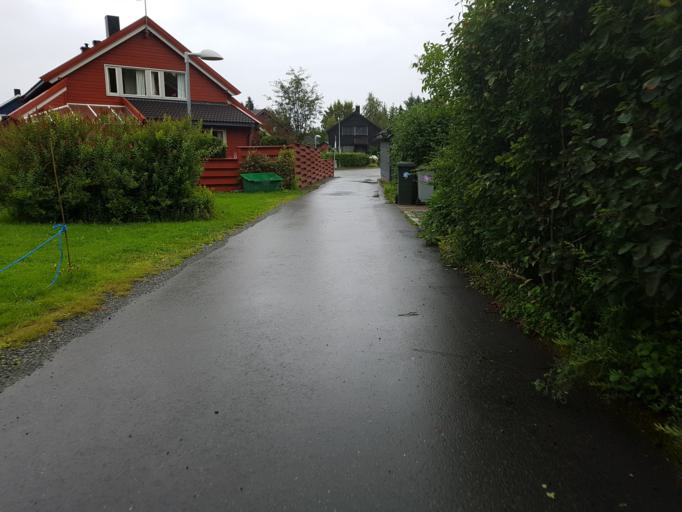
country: NO
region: Sor-Trondelag
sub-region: Trondheim
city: Trondheim
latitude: 63.4012
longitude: 10.4551
